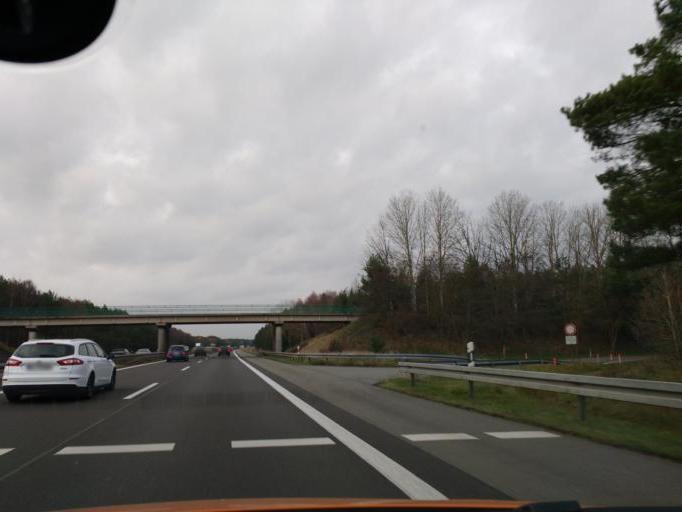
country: DE
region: Brandenburg
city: Walsleben
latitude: 53.0142
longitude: 12.5833
